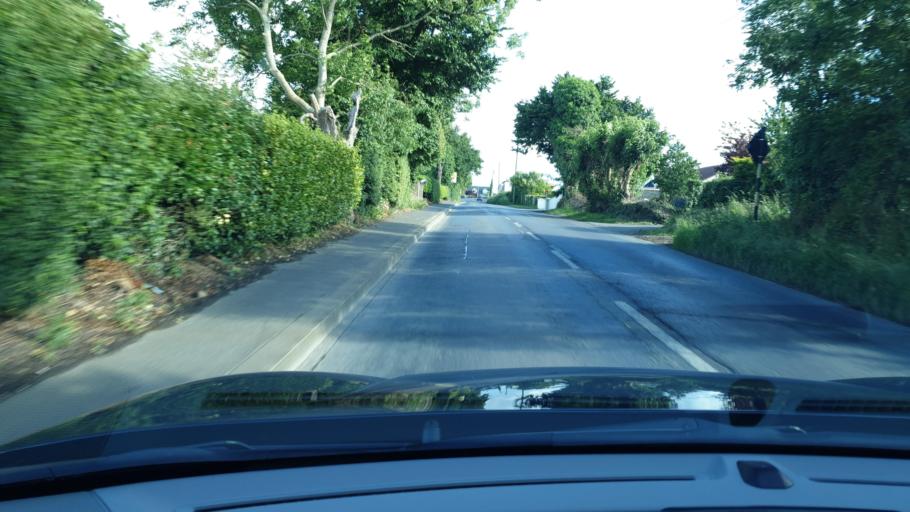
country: IE
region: Leinster
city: An Ros
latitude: 53.5495
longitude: -6.1017
